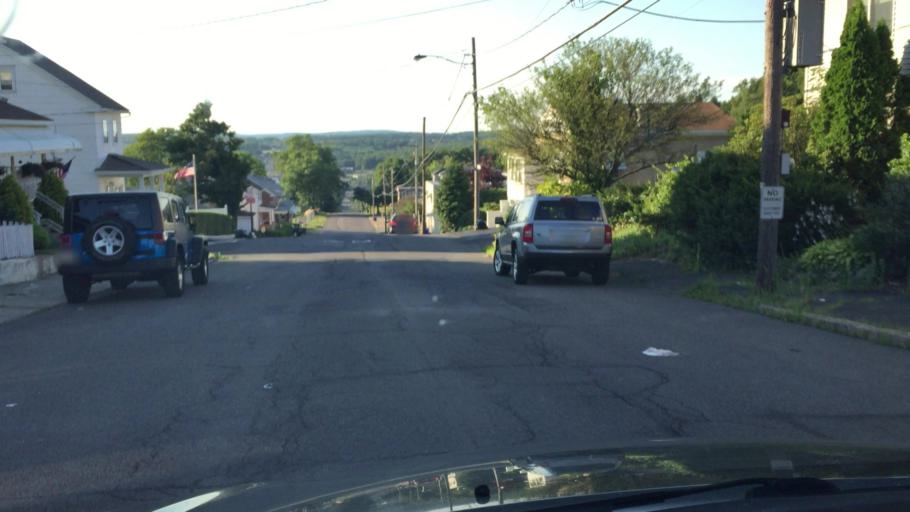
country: US
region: Pennsylvania
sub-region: Luzerne County
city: Hazleton
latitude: 40.9665
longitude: -75.9745
